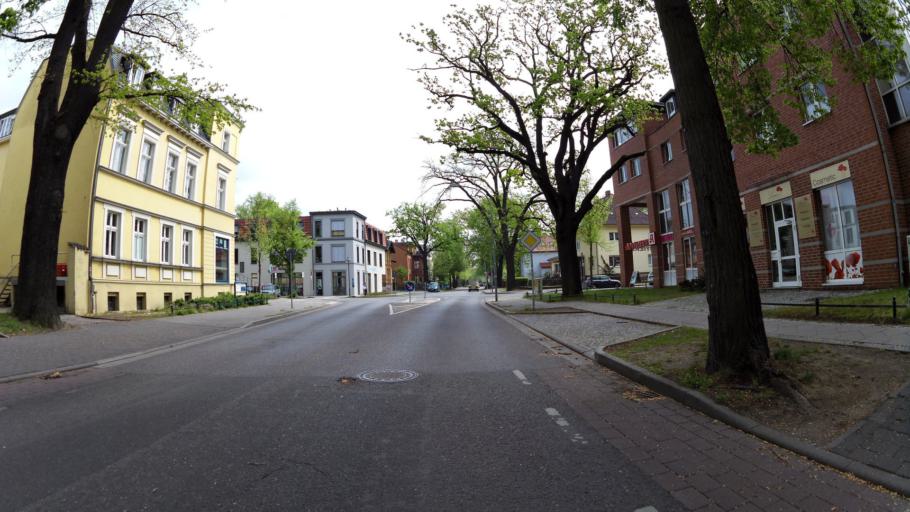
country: DE
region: Brandenburg
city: Konigs Wusterhausen
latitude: 52.2957
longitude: 13.6266
